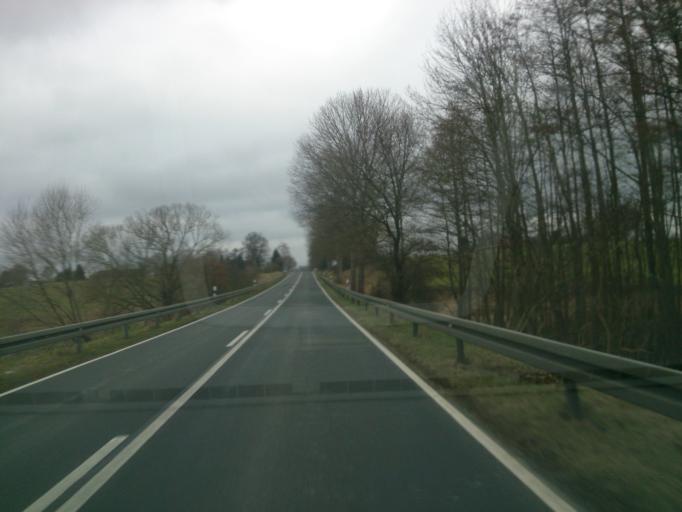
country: DE
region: Mecklenburg-Vorpommern
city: Mollenhagen
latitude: 53.5665
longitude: 12.8625
